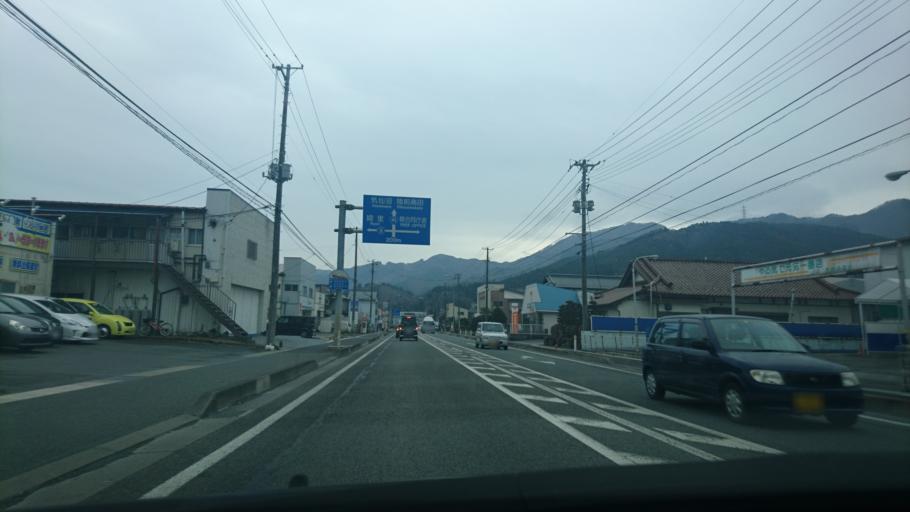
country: JP
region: Iwate
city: Ofunato
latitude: 39.0965
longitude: 141.7073
